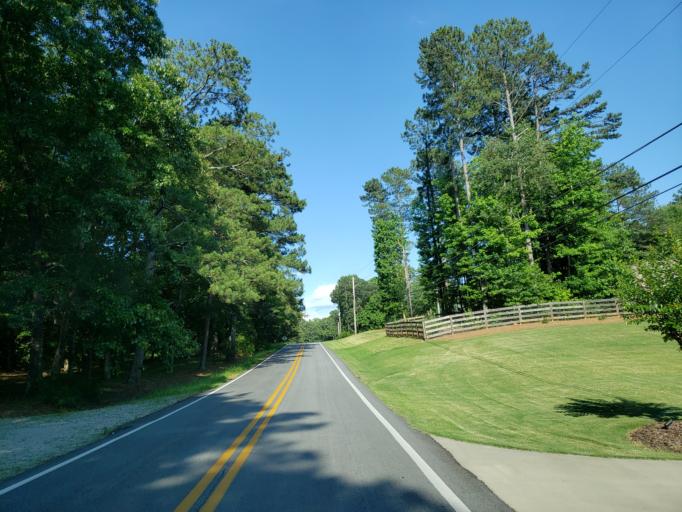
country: US
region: Georgia
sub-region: Haralson County
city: Bremen
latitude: 33.7123
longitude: -85.1241
